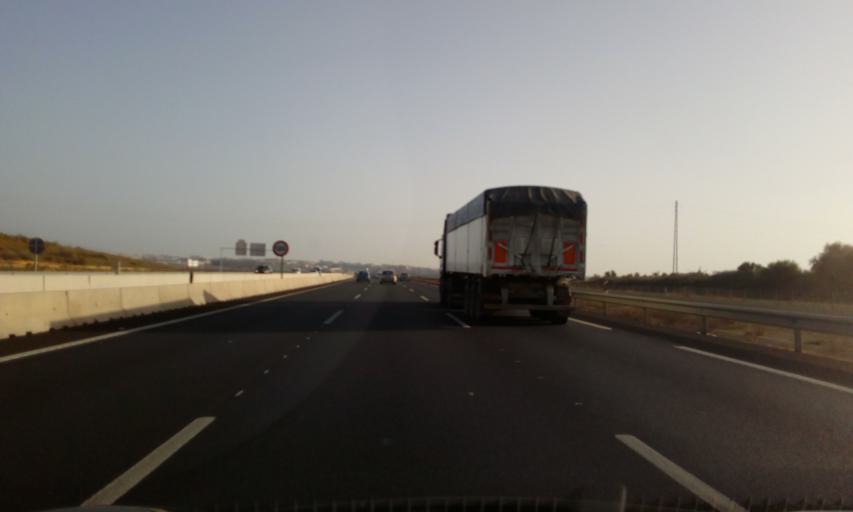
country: ES
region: Andalusia
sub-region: Provincia de Sevilla
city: Espartinas
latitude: 37.3658
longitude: -6.1132
